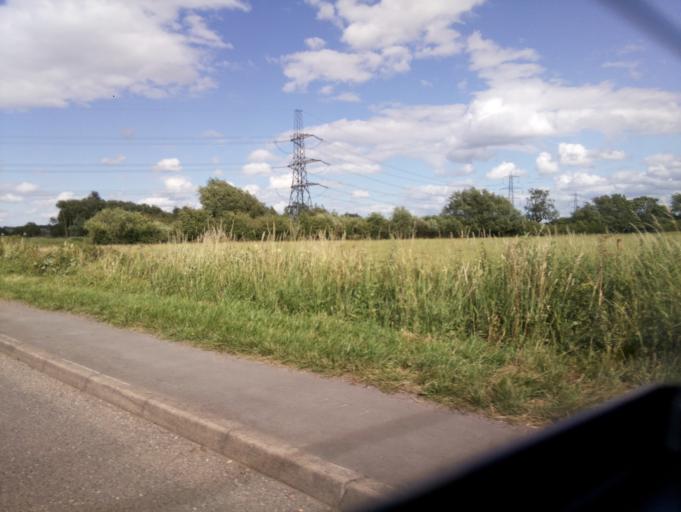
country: GB
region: England
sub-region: Leicestershire
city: Hathern
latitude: 52.8033
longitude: -1.2584
